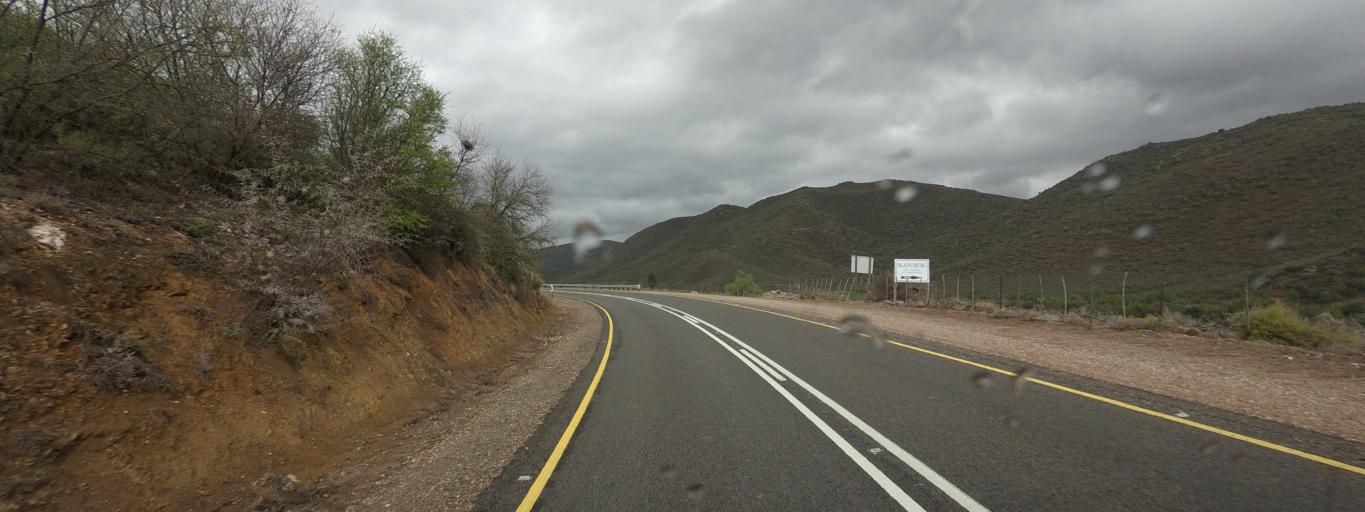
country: ZA
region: Western Cape
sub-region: Eden District Municipality
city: Oudtshoorn
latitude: -33.4076
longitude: 22.2299
